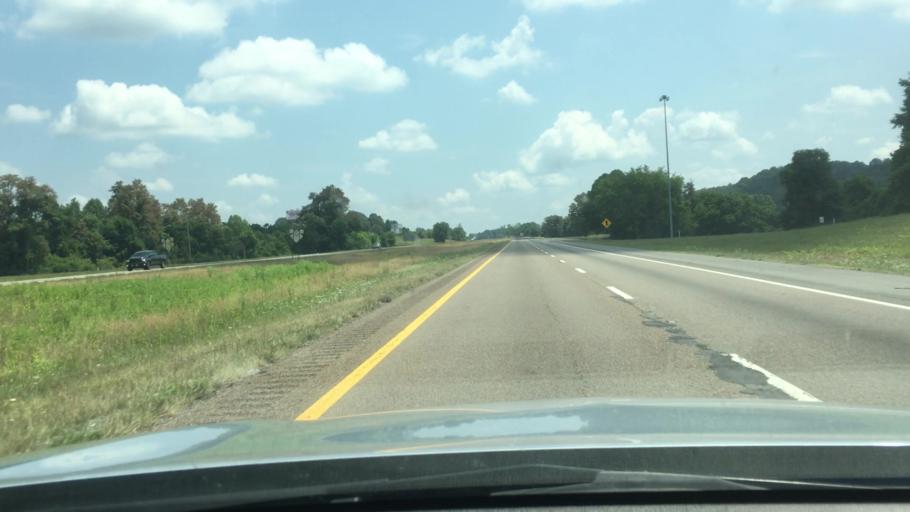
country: US
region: Tennessee
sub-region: Washington County
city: Spurgeon
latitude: 36.5076
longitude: -82.4303
